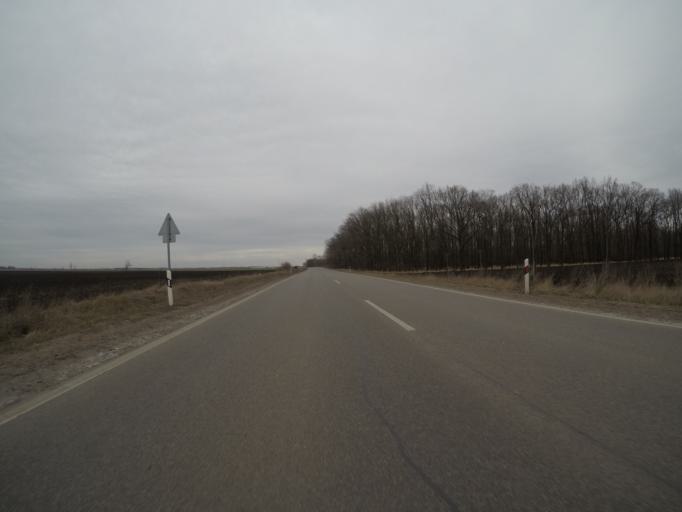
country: HU
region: Jasz-Nagykun-Szolnok
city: Jaszapati
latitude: 47.5108
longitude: 20.0830
